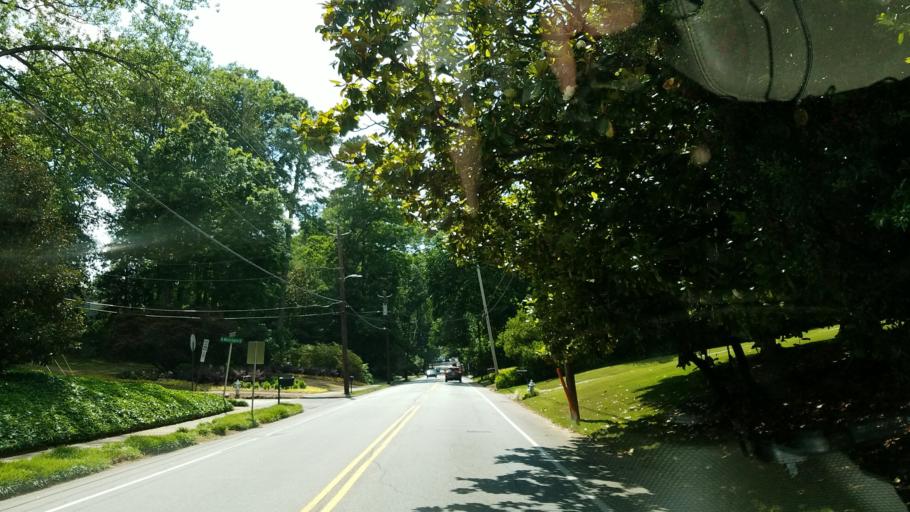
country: US
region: Georgia
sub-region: DeKalb County
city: North Atlanta
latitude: 33.8287
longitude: -84.3912
